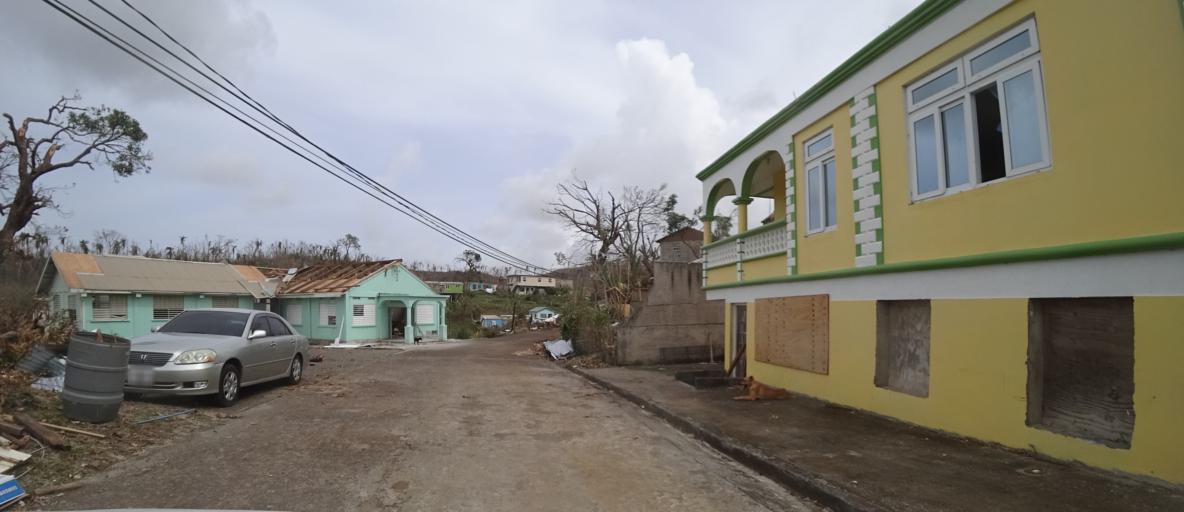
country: DM
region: Saint Andrew
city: Calibishie
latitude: 15.5888
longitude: -61.3760
